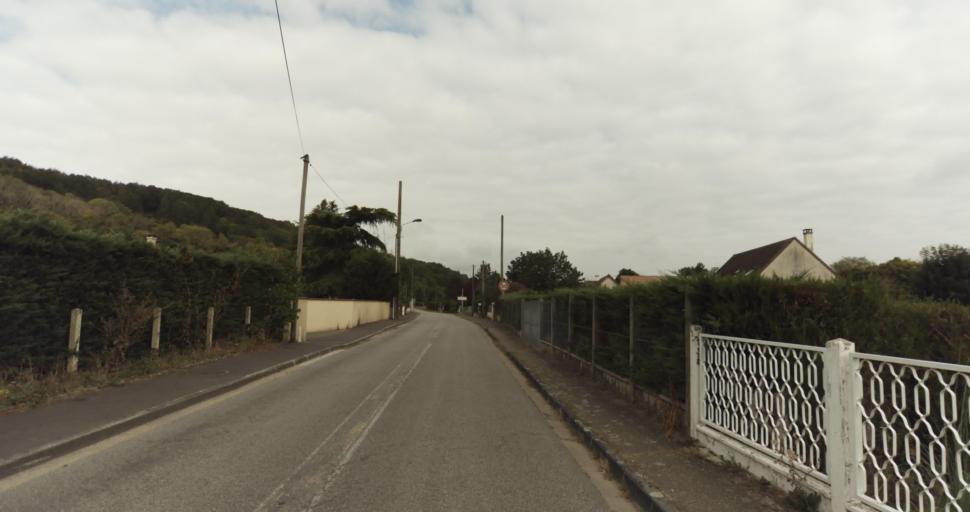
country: FR
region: Haute-Normandie
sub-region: Departement de l'Eure
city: Garennes-sur-Eure
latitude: 48.9176
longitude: 1.4298
